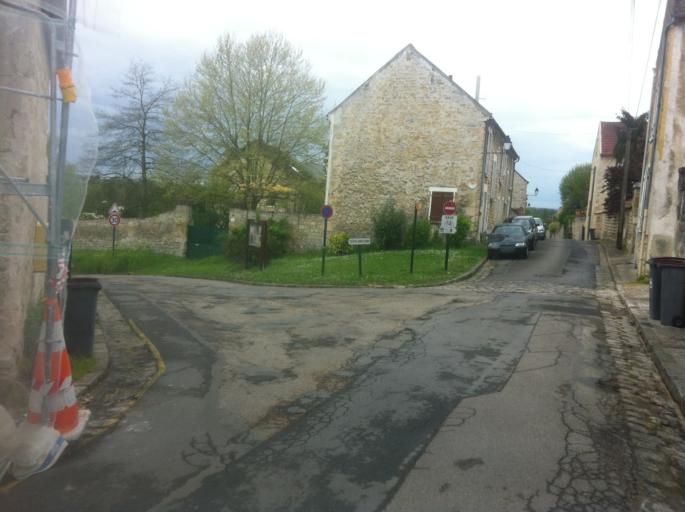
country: FR
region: Ile-de-France
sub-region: Departement du Val-d'Oise
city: Auvers-sur-Oise
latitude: 49.0730
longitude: 2.1809
